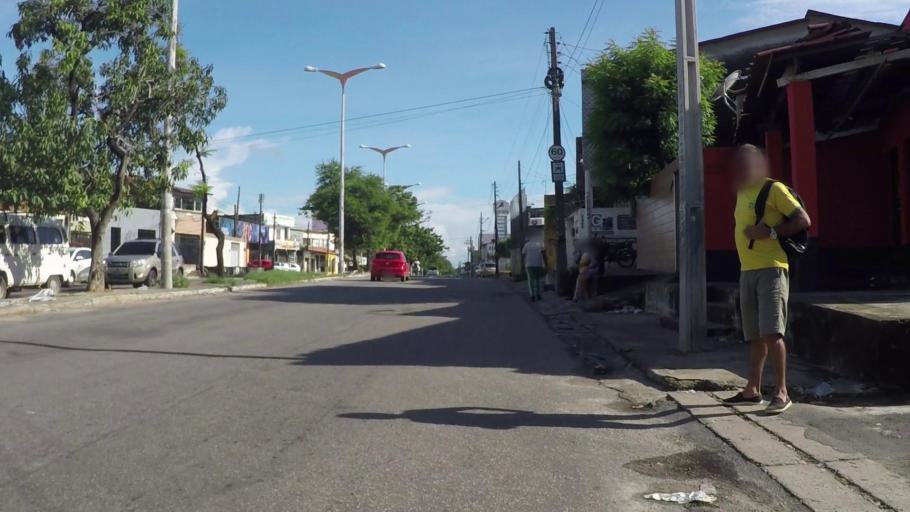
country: BR
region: Ceara
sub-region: Fortaleza
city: Fortaleza
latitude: -3.7284
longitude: -38.5850
